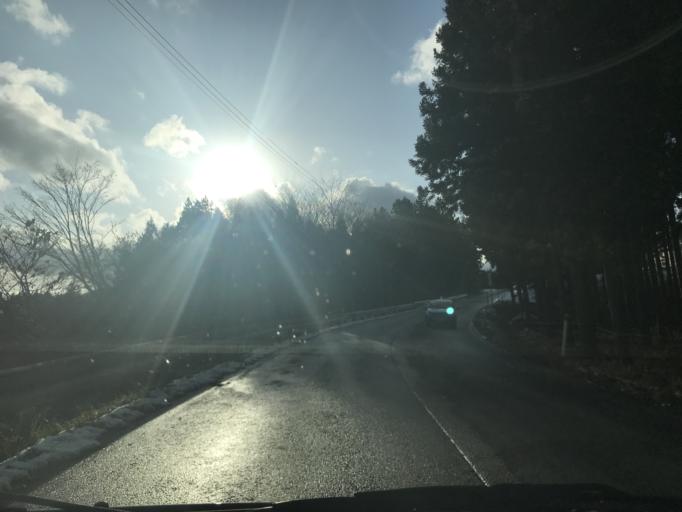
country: JP
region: Iwate
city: Kitakami
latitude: 39.2462
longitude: 141.0068
